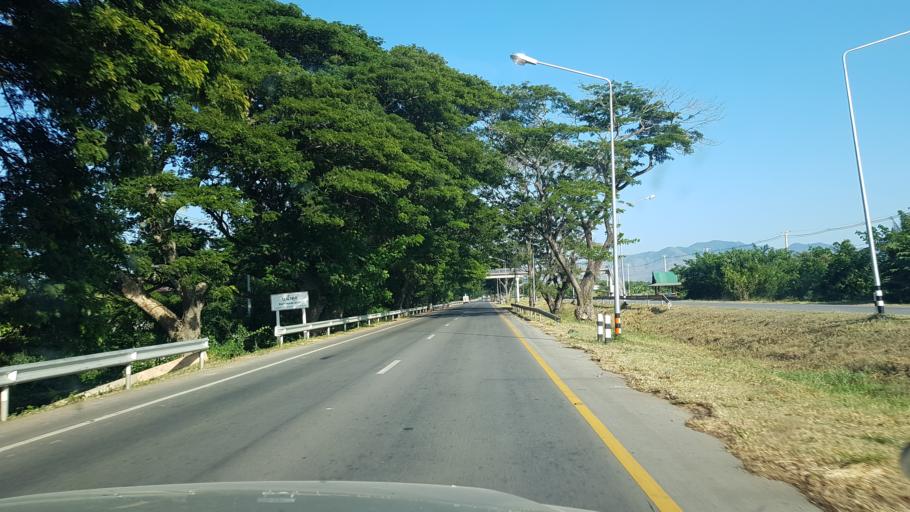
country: TH
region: Phetchabun
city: Lom Sak
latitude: 16.7272
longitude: 101.2602
